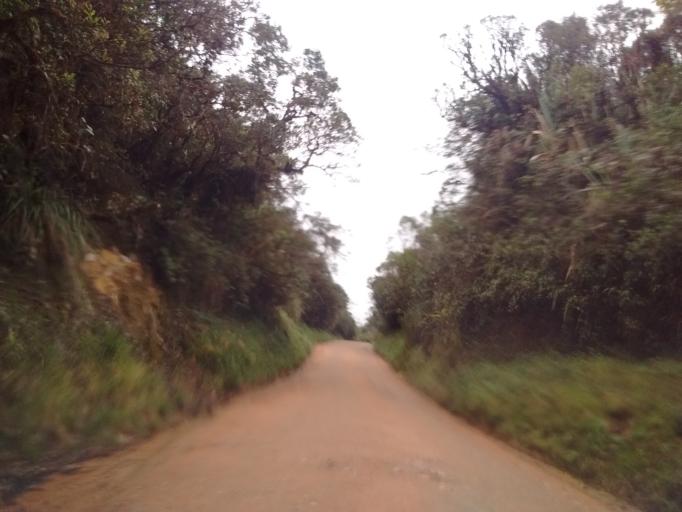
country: CO
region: Huila
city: Isnos
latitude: 2.1165
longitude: -76.3753
